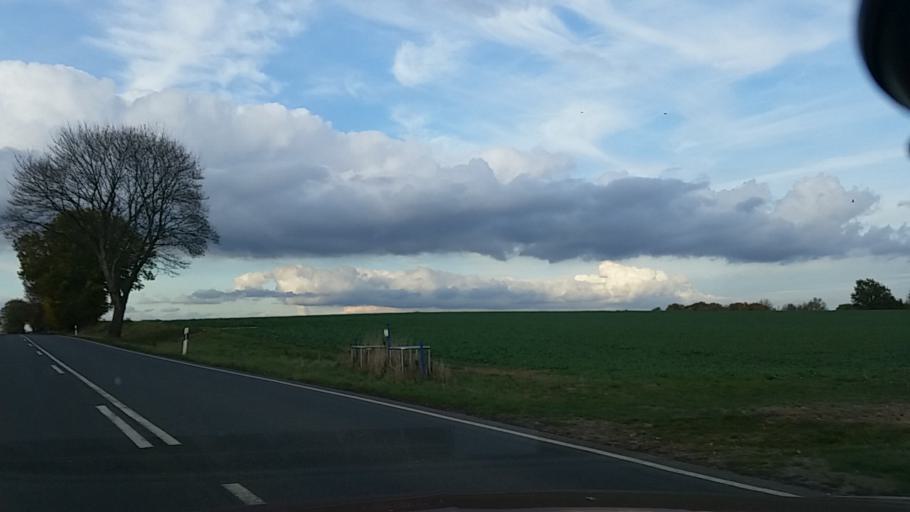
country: DE
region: Lower Saxony
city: Wrestedt
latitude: 52.9389
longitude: 10.5949
